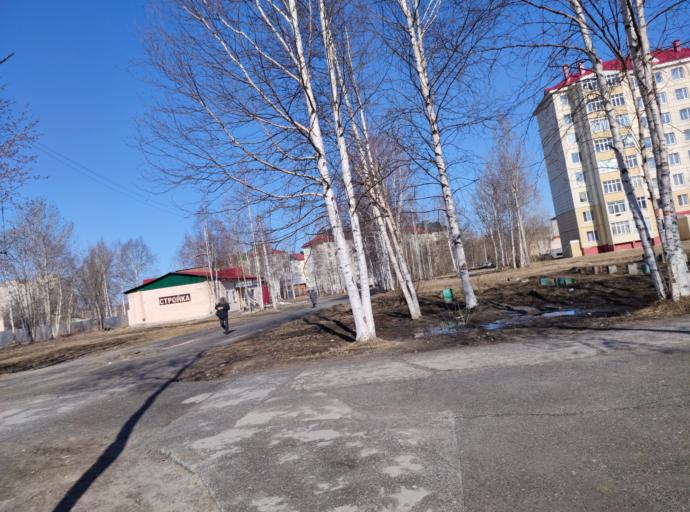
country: RU
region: Khanty-Mansiyskiy Avtonomnyy Okrug
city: Langepas
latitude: 61.2509
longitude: 75.1732
